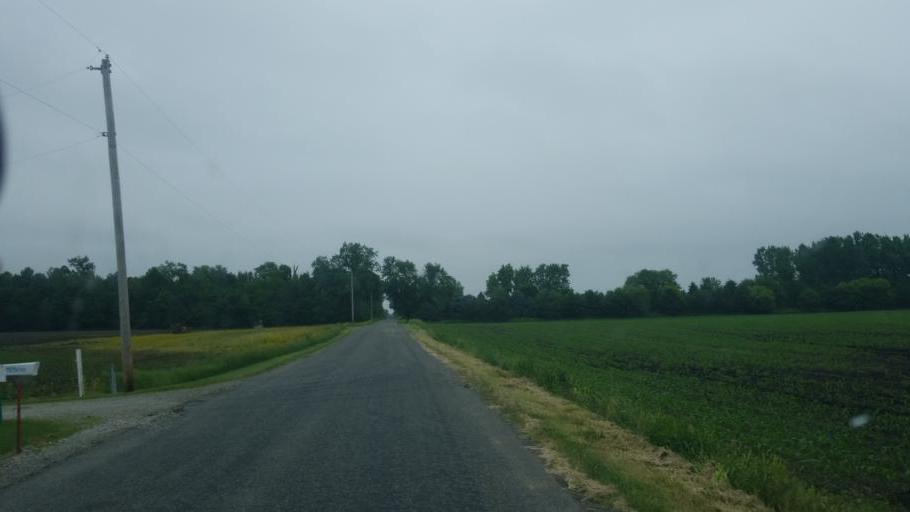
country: US
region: Indiana
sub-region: Marshall County
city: Bremen
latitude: 41.5020
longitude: -86.1370
